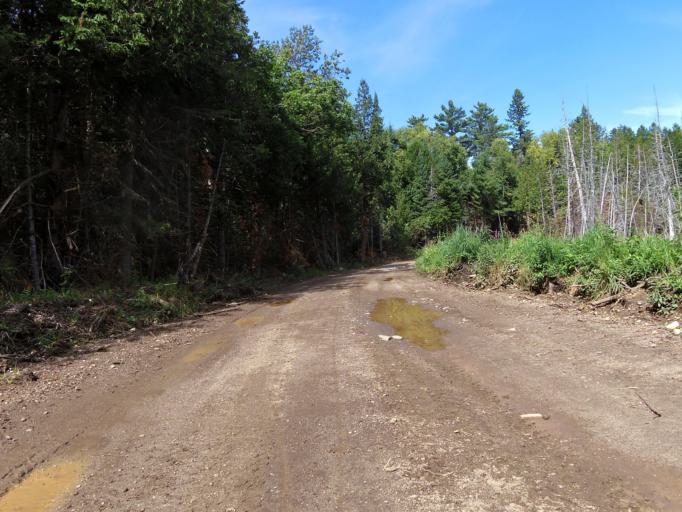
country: CA
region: Ontario
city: Renfrew
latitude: 45.1078
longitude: -76.7240
